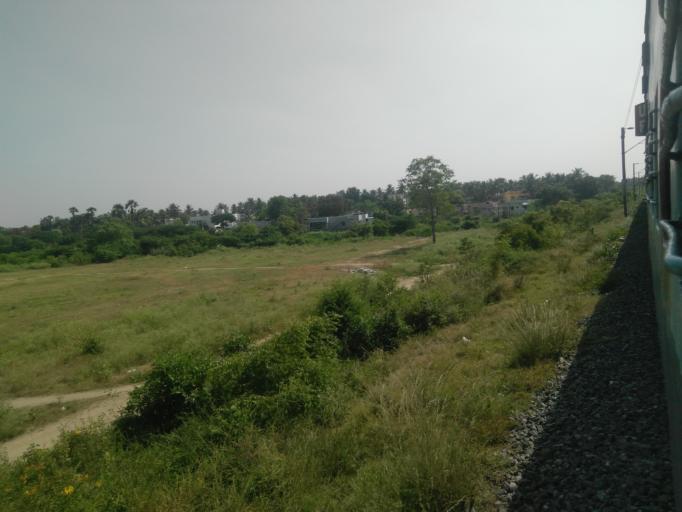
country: IN
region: Tamil Nadu
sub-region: Coimbatore
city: Periyanayakkanpalaiyam
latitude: 11.0994
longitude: 76.9481
